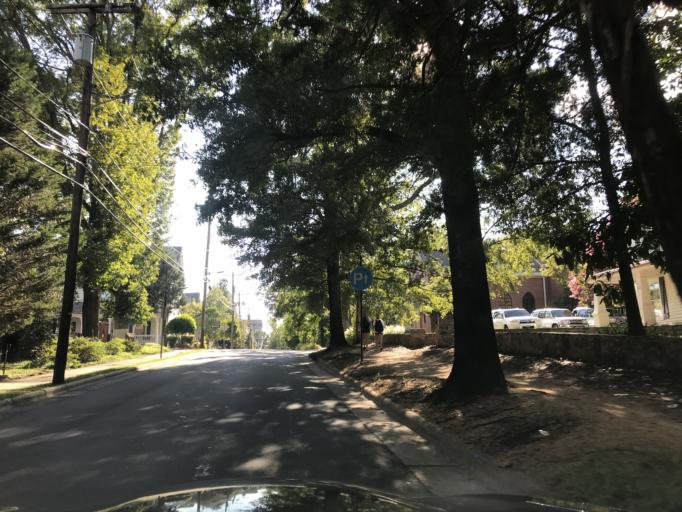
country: US
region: North Carolina
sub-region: Orange County
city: Chapel Hill
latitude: 35.9163
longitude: -79.0506
